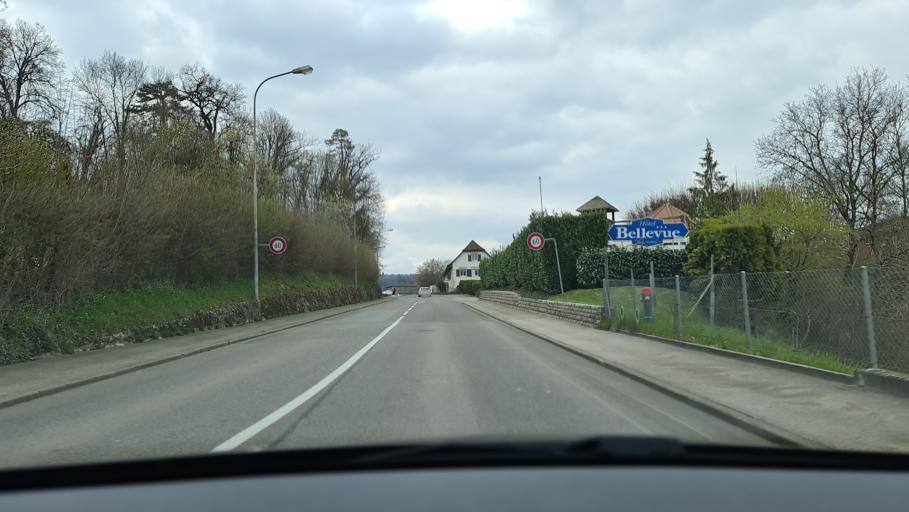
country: CH
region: Jura
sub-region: Porrentruy District
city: Porrentruy
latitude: 47.4234
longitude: 7.0774
